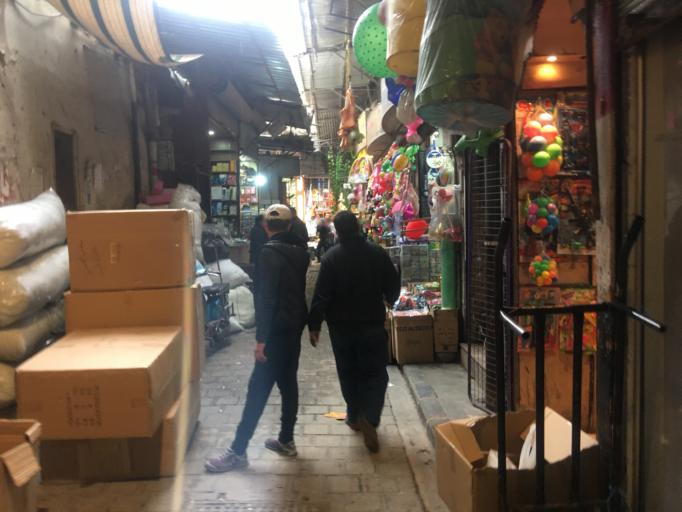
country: SY
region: Dimashq
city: Damascus
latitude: 33.5120
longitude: 36.3043
